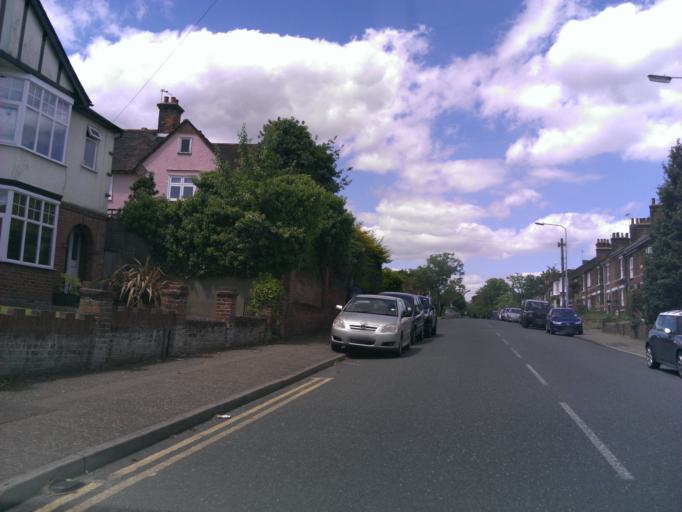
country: GB
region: England
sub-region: Essex
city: Colchester
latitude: 51.8779
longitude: 0.9186
